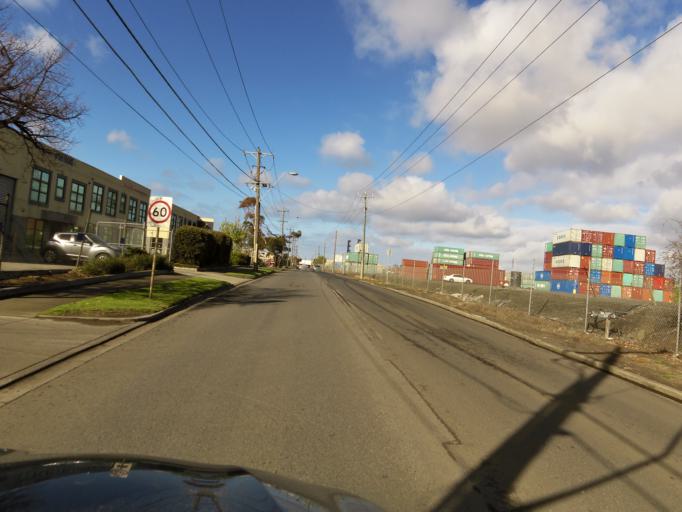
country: AU
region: Victoria
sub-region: Maribyrnong
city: Kingsville
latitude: -37.8057
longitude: 144.8616
